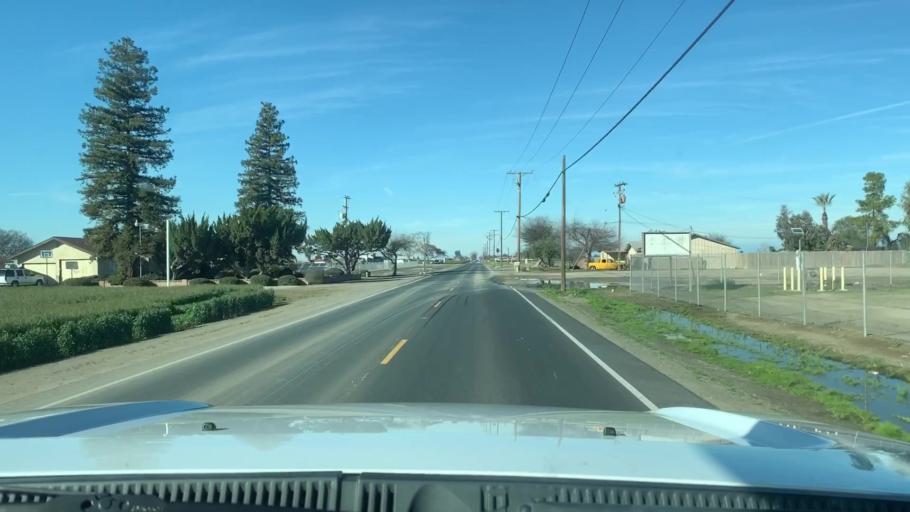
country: US
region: California
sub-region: Kings County
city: Corcoran
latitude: 36.1876
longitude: -119.4932
